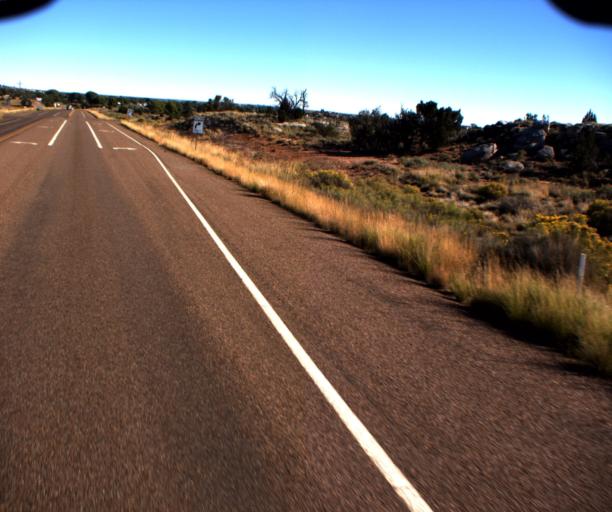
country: US
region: Arizona
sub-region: Navajo County
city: Taylor
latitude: 34.4468
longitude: -110.0939
